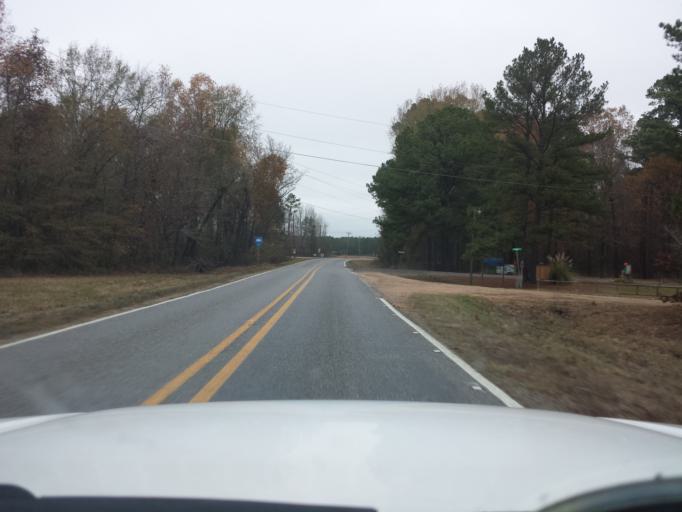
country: US
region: Mississippi
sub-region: Madison County
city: Canton
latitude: 32.4835
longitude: -89.9187
